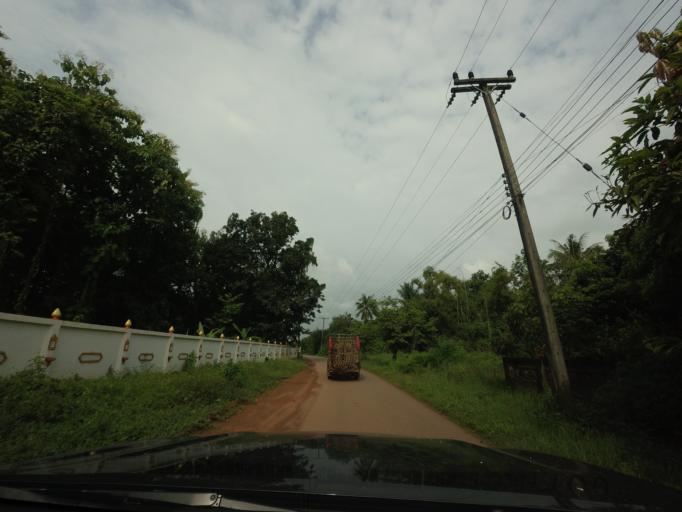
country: TH
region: Nong Khai
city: Nong Khai
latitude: 17.8168
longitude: 102.7171
